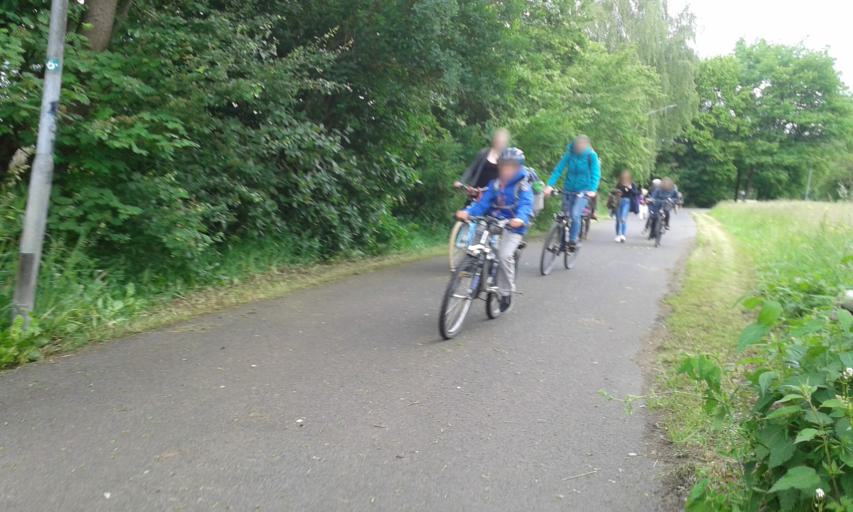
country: DE
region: Bavaria
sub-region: Regierungsbezirk Mittelfranken
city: Hersbruck
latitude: 49.5037
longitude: 11.4342
